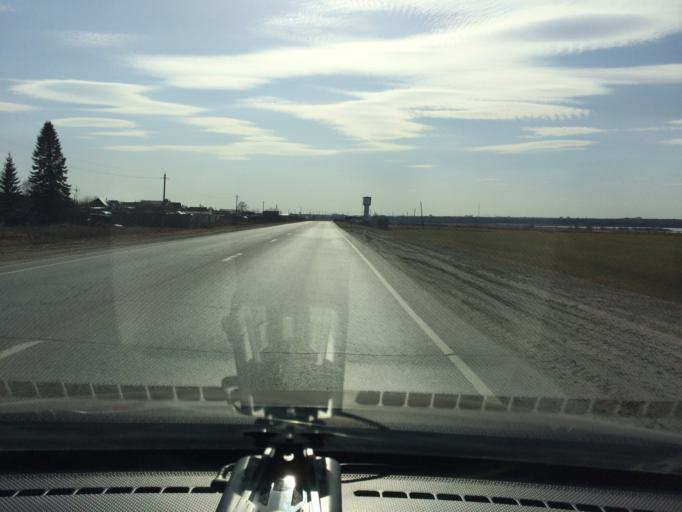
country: RU
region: Mariy-El
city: Yoshkar-Ola
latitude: 56.6621
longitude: 47.9799
